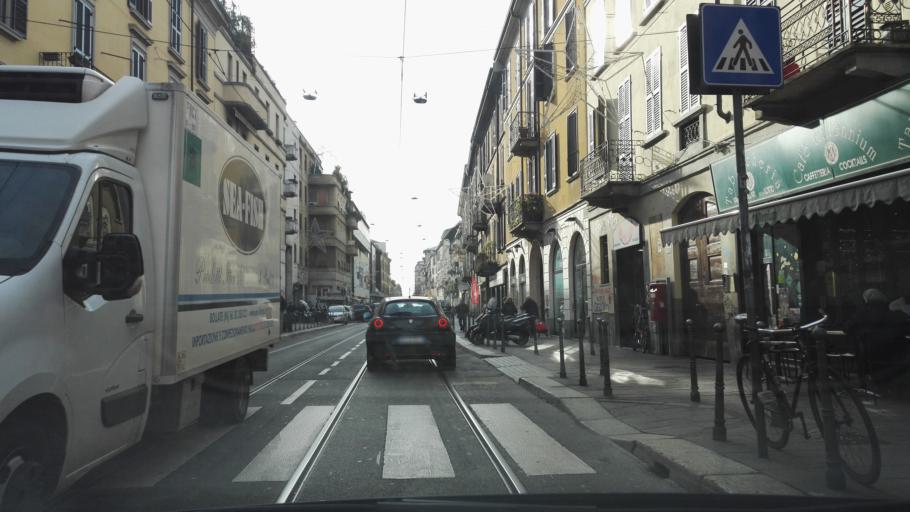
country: IT
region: Lombardy
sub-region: Citta metropolitana di Milano
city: Milano
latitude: 45.4503
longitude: 9.1799
